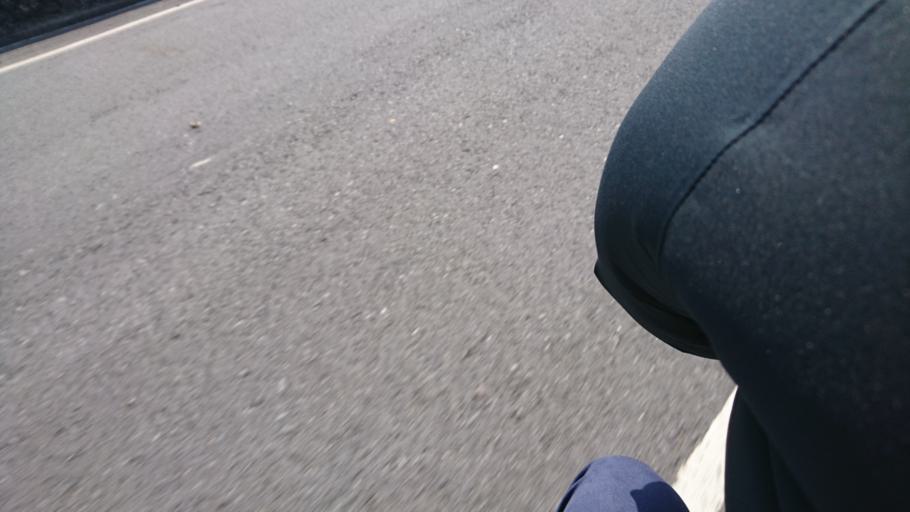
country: TW
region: Taiwan
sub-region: Miaoli
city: Miaoli
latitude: 24.6937
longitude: 120.8593
